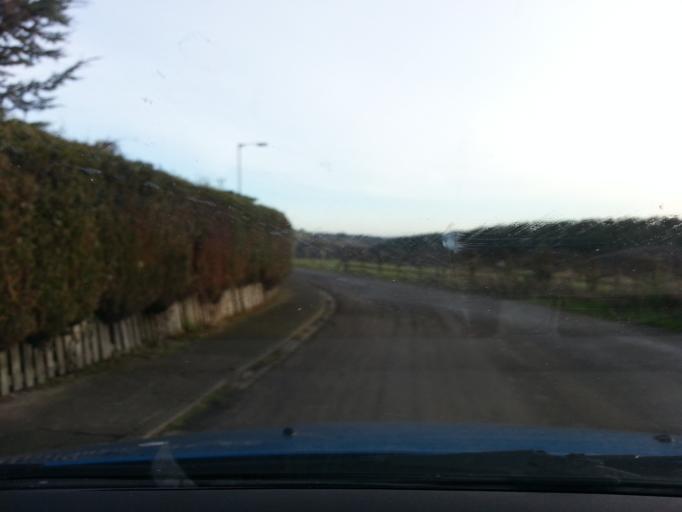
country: GB
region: England
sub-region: County Durham
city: Crook
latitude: 54.7258
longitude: -1.7610
